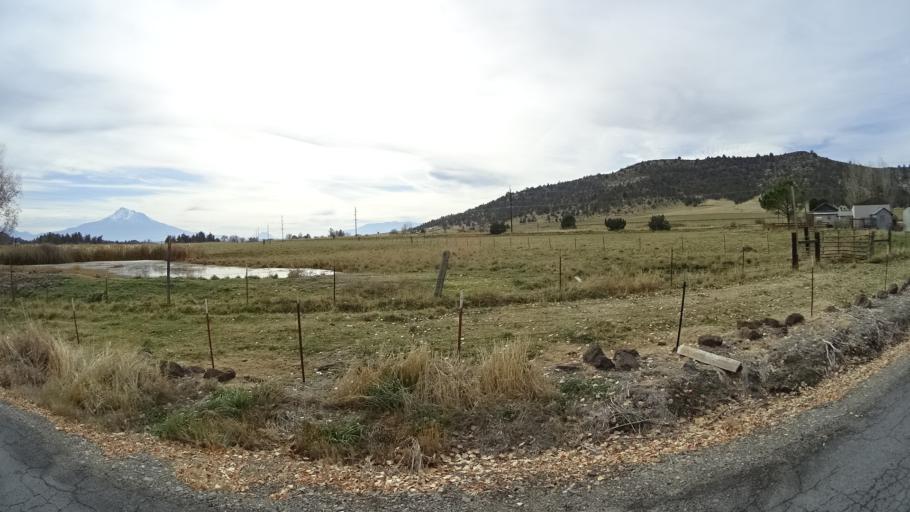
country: US
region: California
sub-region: Siskiyou County
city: Montague
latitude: 41.6833
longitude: -122.5307
